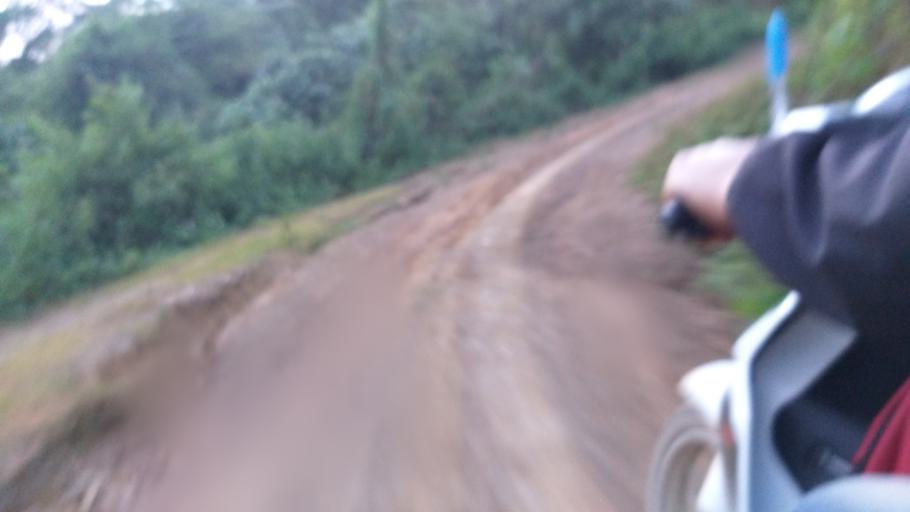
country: LA
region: Phongsali
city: Khoa
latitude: 21.4275
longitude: 102.6303
